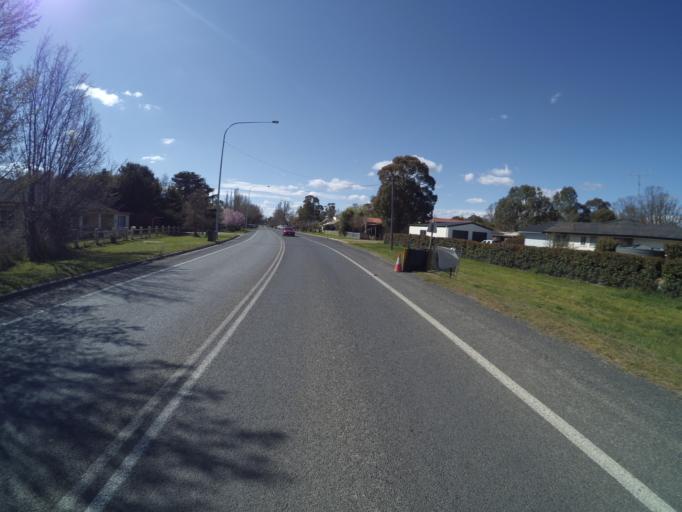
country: AU
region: New South Wales
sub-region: Palerang
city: Bungendore
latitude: -35.2578
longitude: 149.4375
